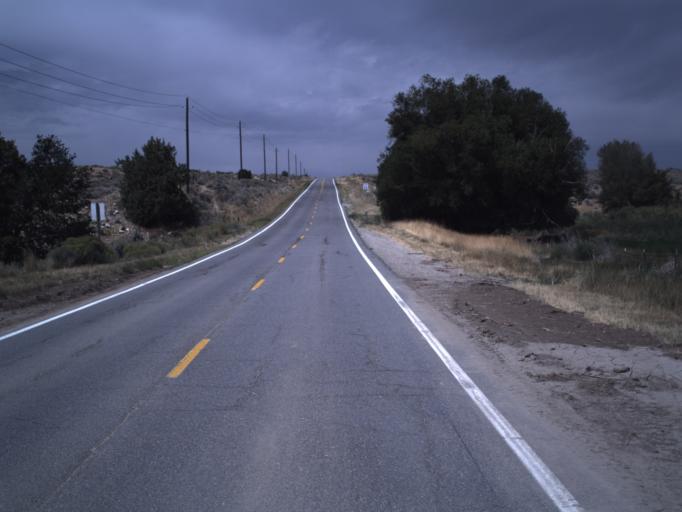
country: US
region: Utah
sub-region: Tooele County
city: Tooele
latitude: 40.3439
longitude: -112.3051
